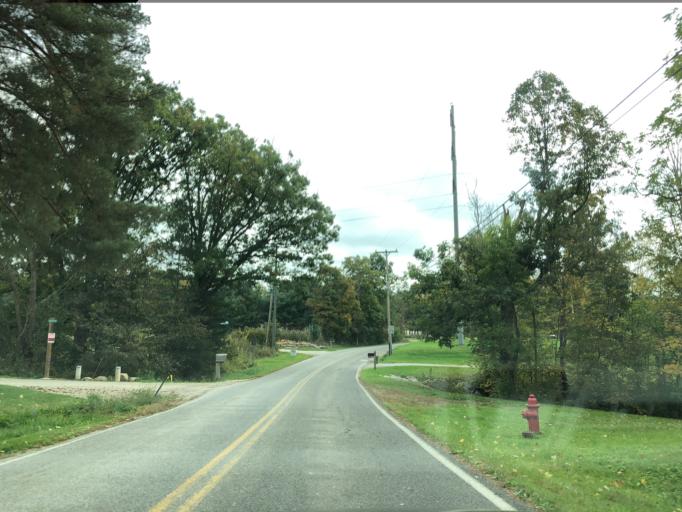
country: US
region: Ohio
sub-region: Summit County
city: Boston Heights
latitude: 41.2723
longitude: -81.5255
